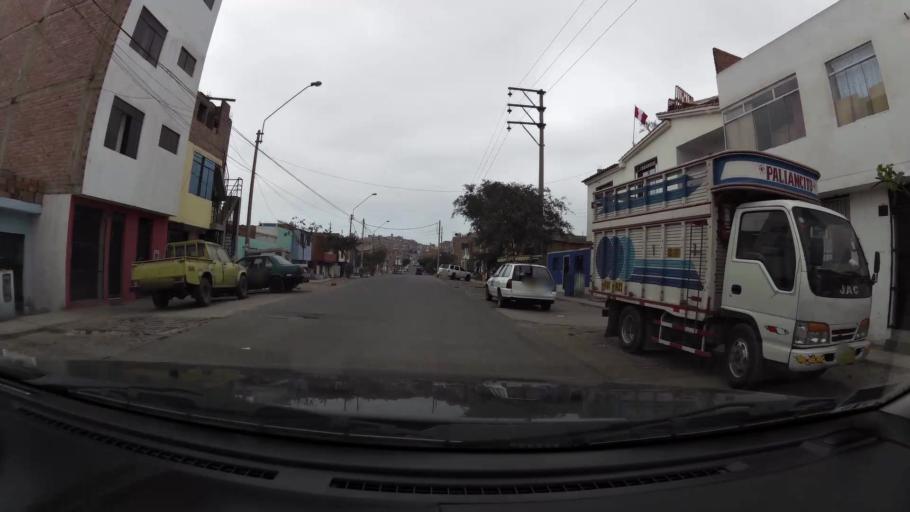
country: PE
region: Lima
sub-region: Lima
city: Surco
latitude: -12.1977
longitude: -76.9835
